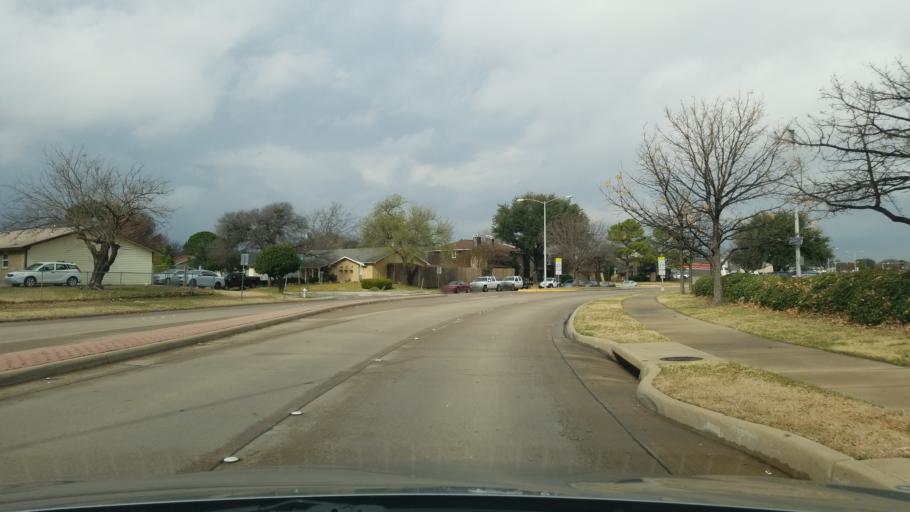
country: US
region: Texas
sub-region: Denton County
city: Lewisville
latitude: 33.0383
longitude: -97.0202
